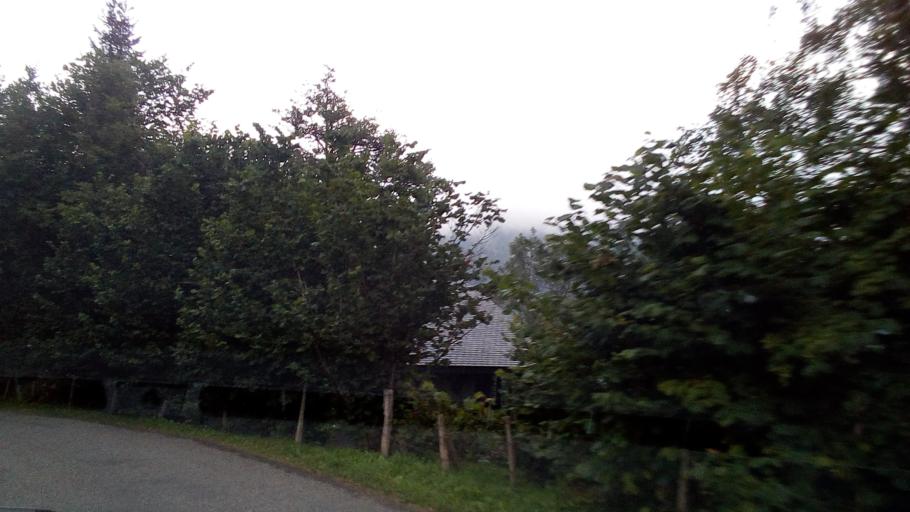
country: FR
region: Midi-Pyrenees
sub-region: Departement des Hautes-Pyrenees
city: Cauterets
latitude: 42.9463
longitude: -0.1882
